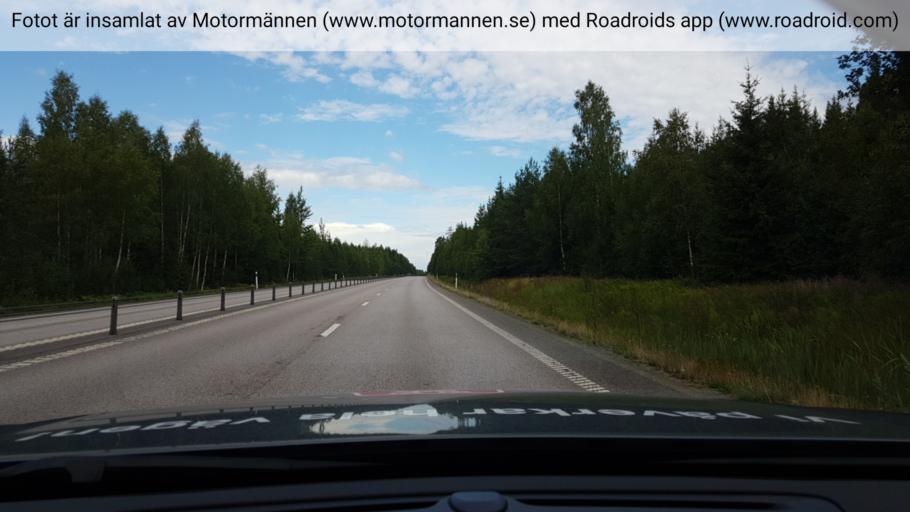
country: SE
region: Uppsala
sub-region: Heby Kommun
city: Tarnsjo
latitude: 60.2606
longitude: 16.9482
